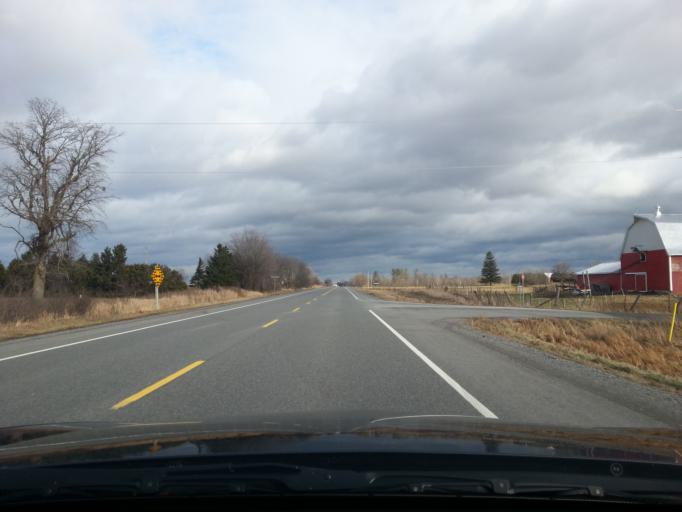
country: CA
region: Ontario
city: Prescott
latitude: 45.0662
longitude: -75.4292
